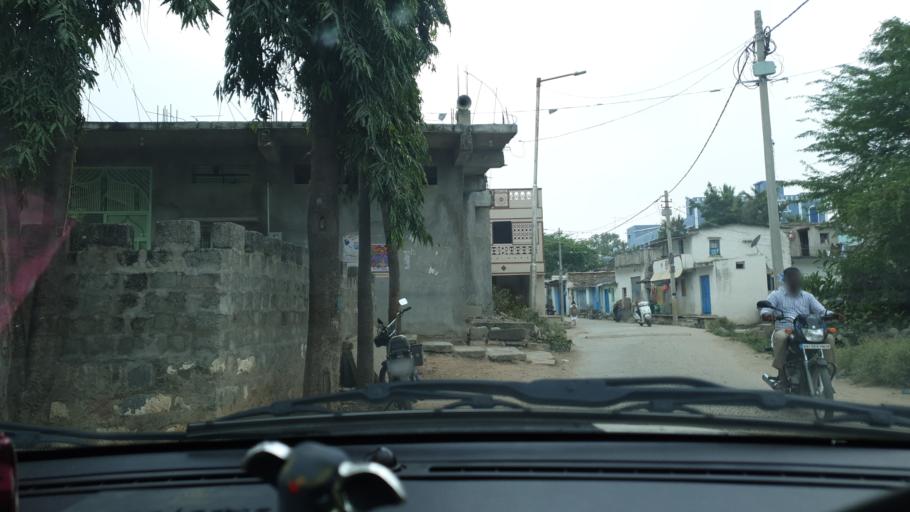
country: IN
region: Karnataka
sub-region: Yadgir
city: Gurmatkal
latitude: 16.8645
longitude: 77.3929
